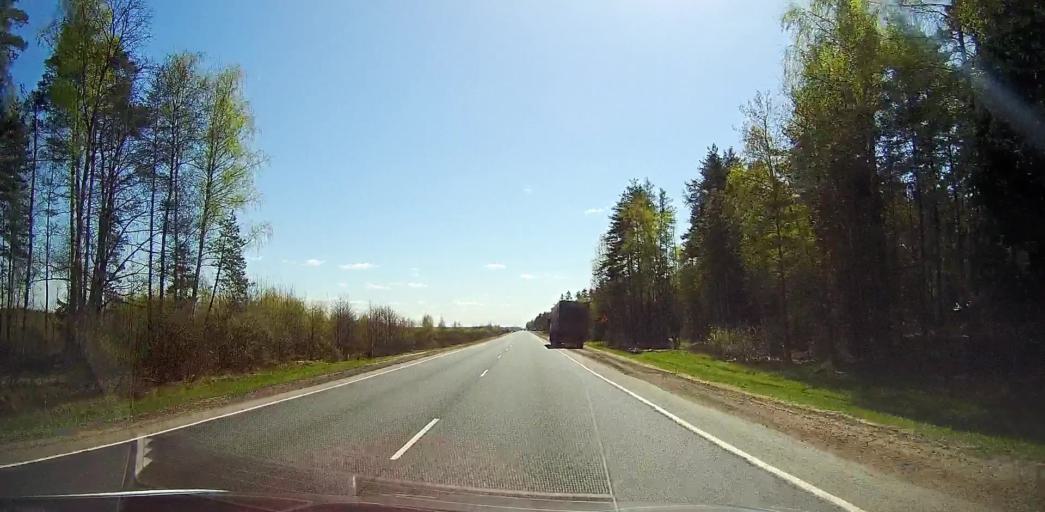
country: RU
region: Moskovskaya
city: Gzhel'
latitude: 55.5997
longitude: 38.3789
